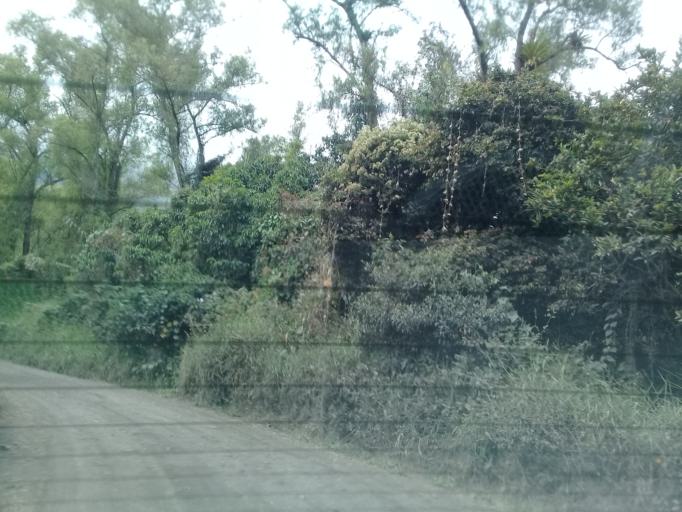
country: CO
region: Cundinamarca
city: Une
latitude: 4.4106
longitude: -73.9889
